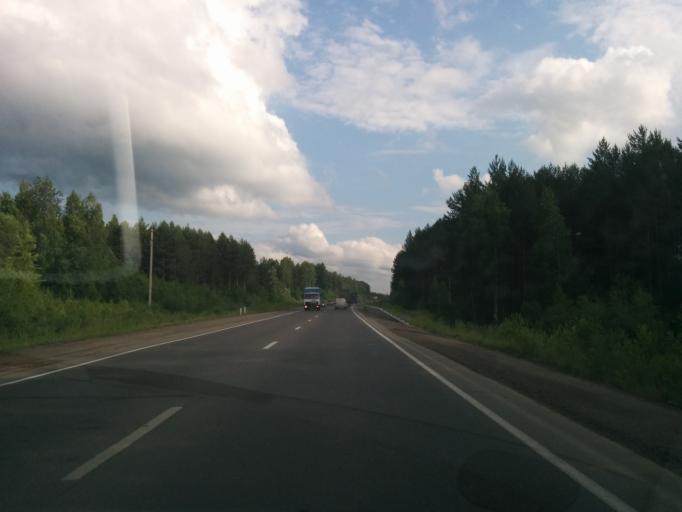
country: RU
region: Perm
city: Polazna
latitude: 58.1255
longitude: 56.4229
